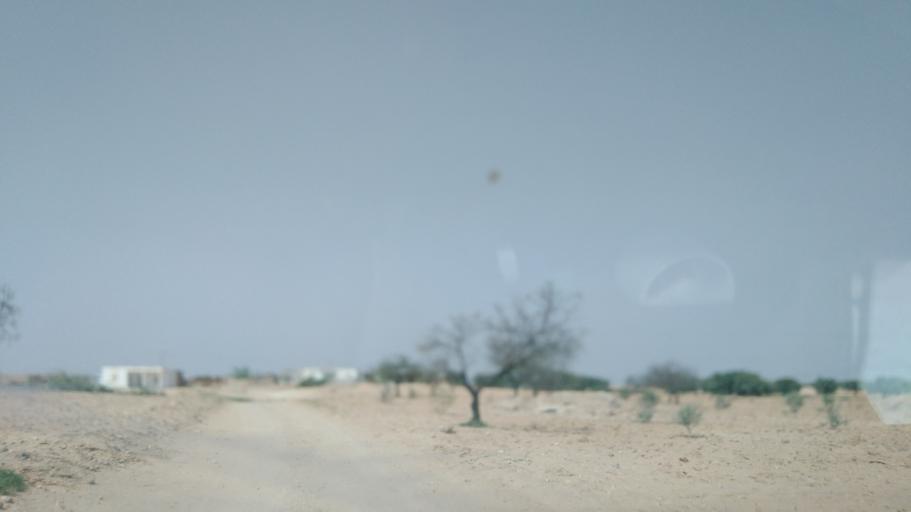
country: TN
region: Safaqis
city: Sfax
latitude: 34.6401
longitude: 10.5654
